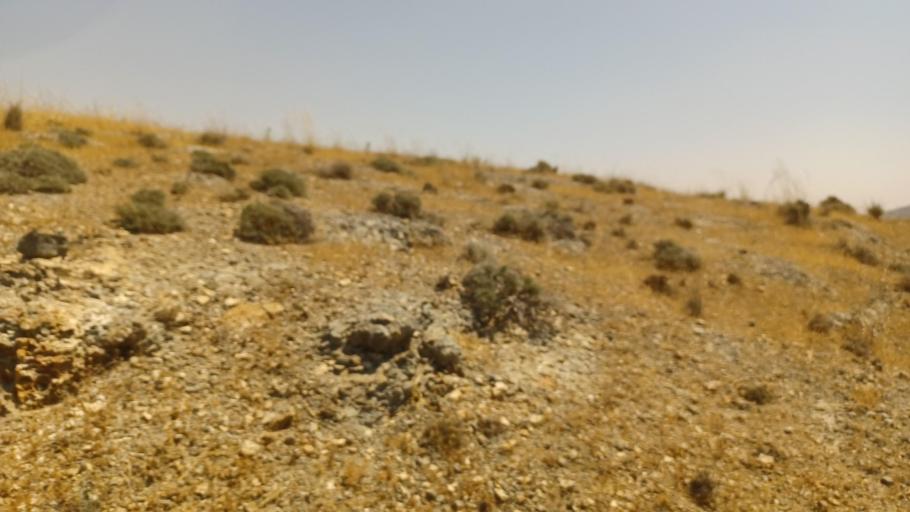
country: CY
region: Larnaka
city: Troulloi
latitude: 35.0009
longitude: 33.6144
